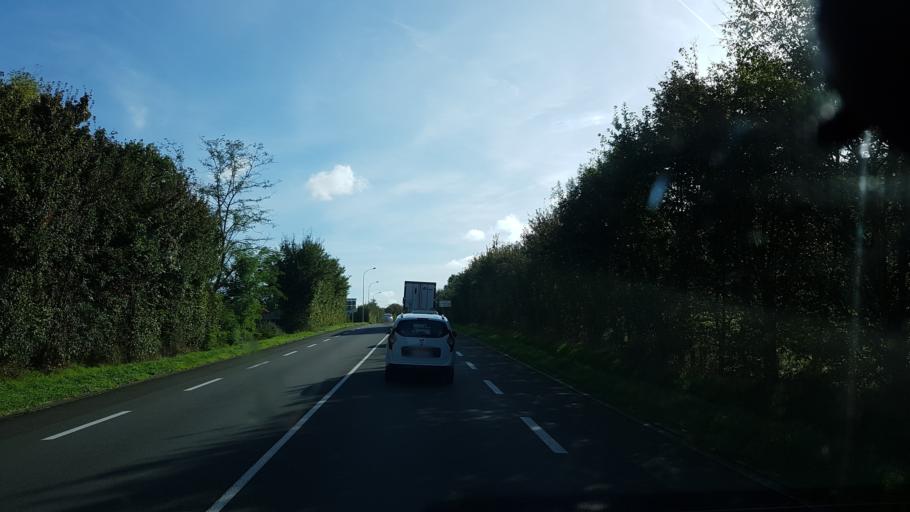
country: FR
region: Poitou-Charentes
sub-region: Departement de la Charente
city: Saint-Claud
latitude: 45.8845
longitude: 0.4693
